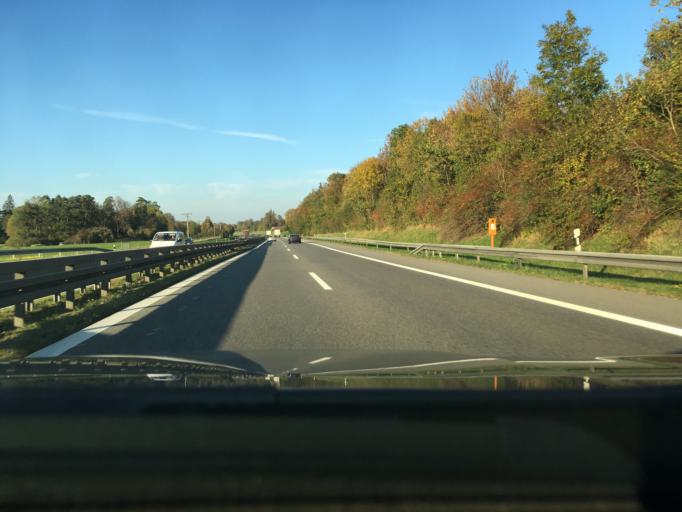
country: DE
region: Baden-Wuerttemberg
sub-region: Tuebingen Region
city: Aitrach
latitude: 47.9436
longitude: 10.1014
